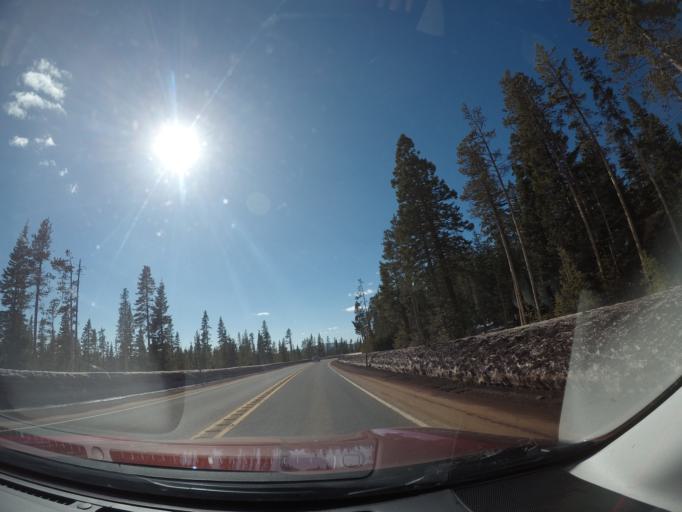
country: US
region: Oregon
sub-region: Deschutes County
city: Sunriver
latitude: 43.9815
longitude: -121.5827
